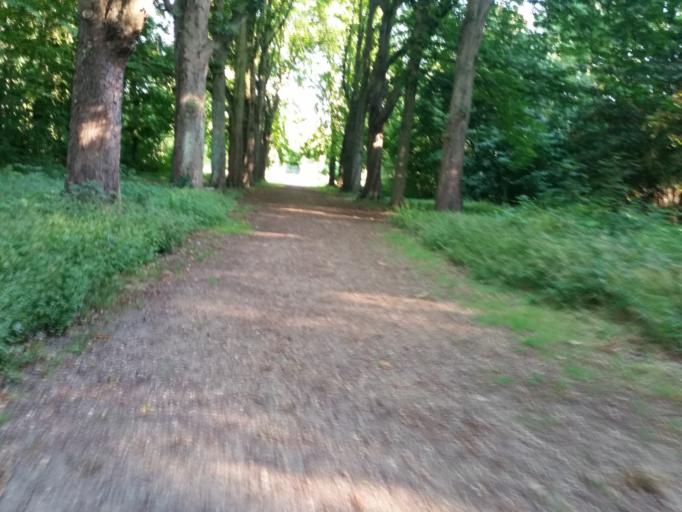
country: BE
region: Flanders
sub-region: Provincie Antwerpen
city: Mechelen
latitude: 51.0231
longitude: 4.4569
